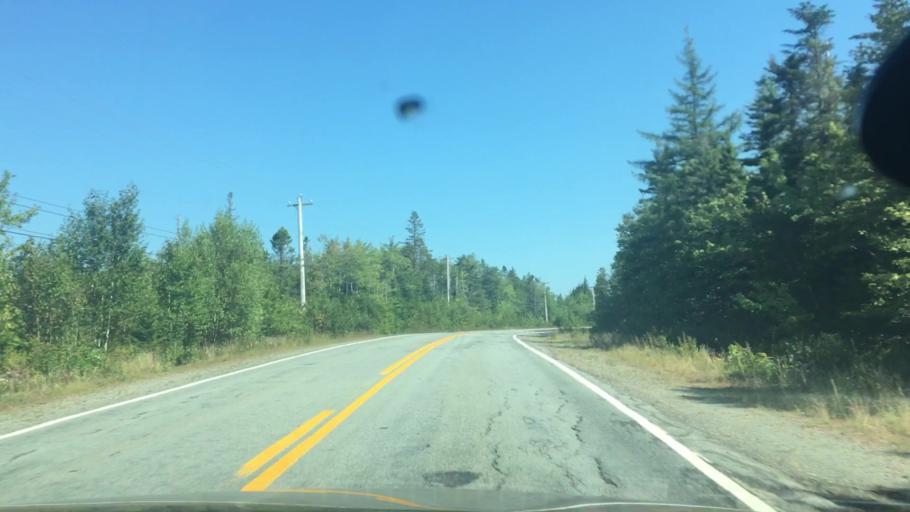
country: CA
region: Nova Scotia
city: New Glasgow
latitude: 44.9079
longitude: -62.5554
